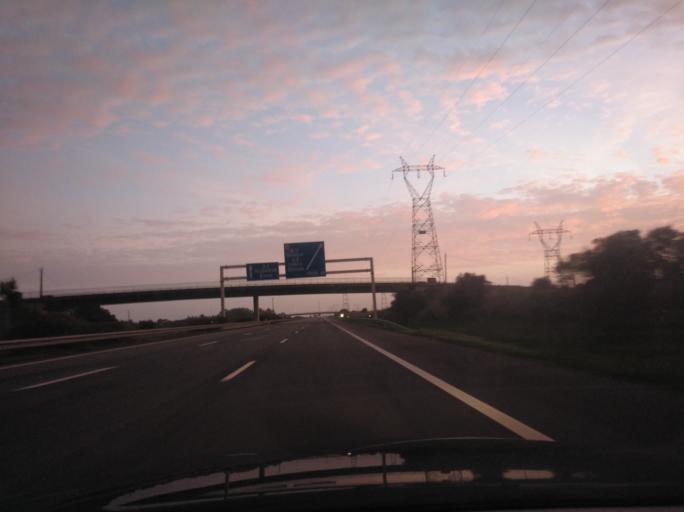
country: PT
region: Setubal
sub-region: Palmela
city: Palmela
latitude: 38.6001
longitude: -8.8662
